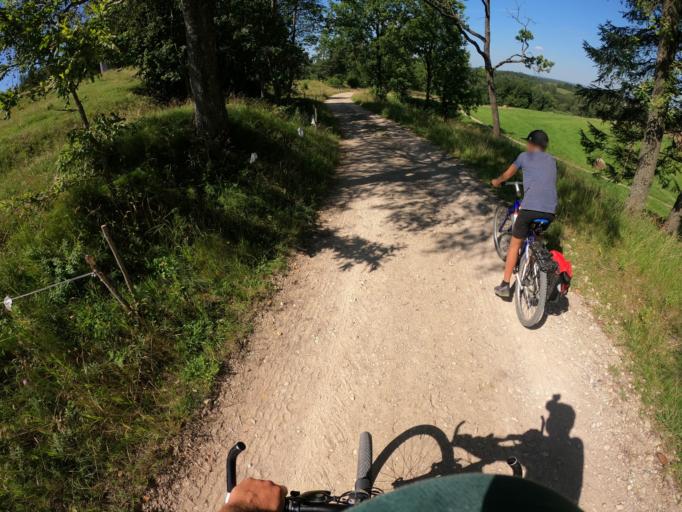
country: LT
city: Varniai
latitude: 55.8722
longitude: 22.5560
